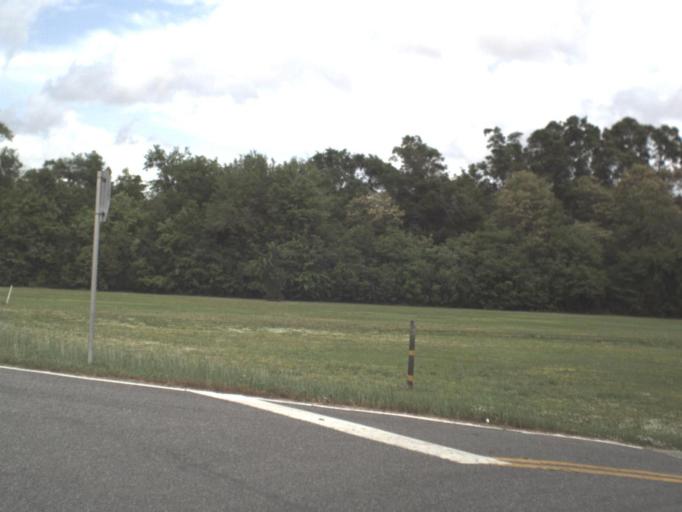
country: US
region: Florida
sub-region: Santa Rosa County
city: Point Baker
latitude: 30.7234
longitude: -87.0788
